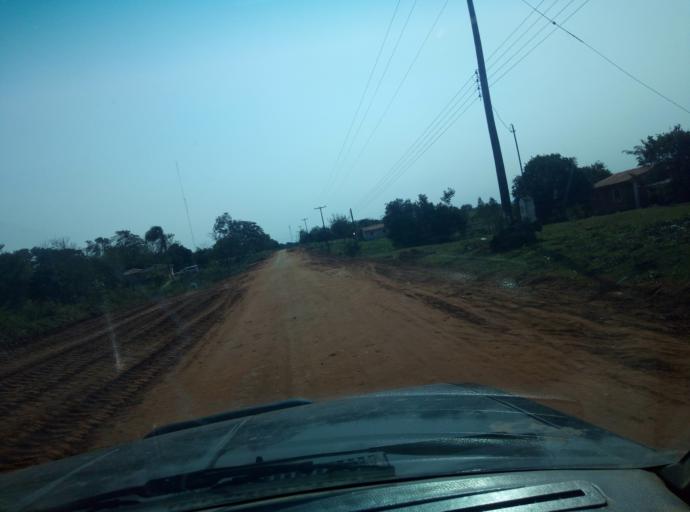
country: PY
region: Caaguazu
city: Carayao
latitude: -25.3258
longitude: -56.3302
